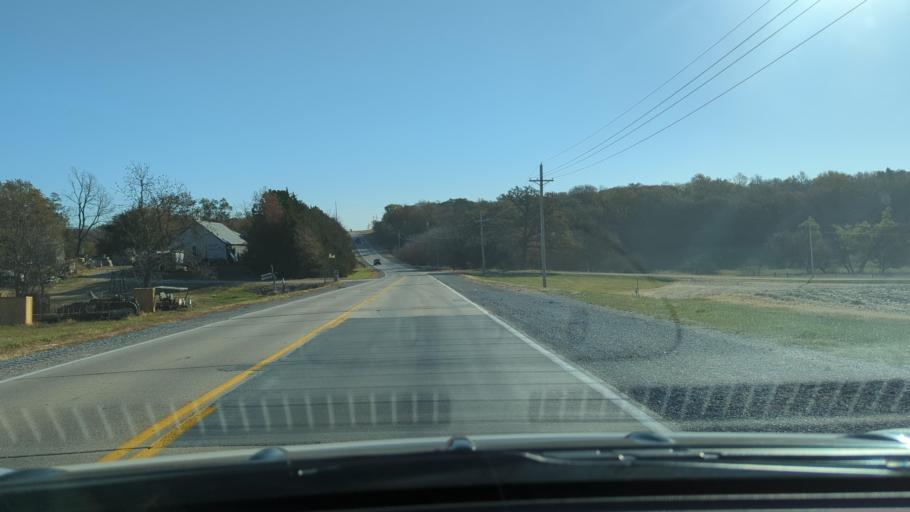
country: US
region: Nebraska
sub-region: Sarpy County
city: Offutt Air Force Base
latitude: 41.0927
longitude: -95.9936
